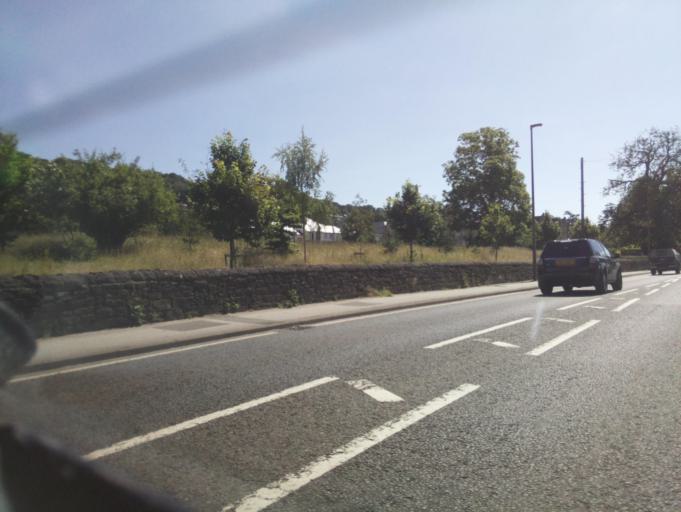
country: GB
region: England
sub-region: Derbyshire
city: Matlock
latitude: 53.1567
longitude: -1.5839
